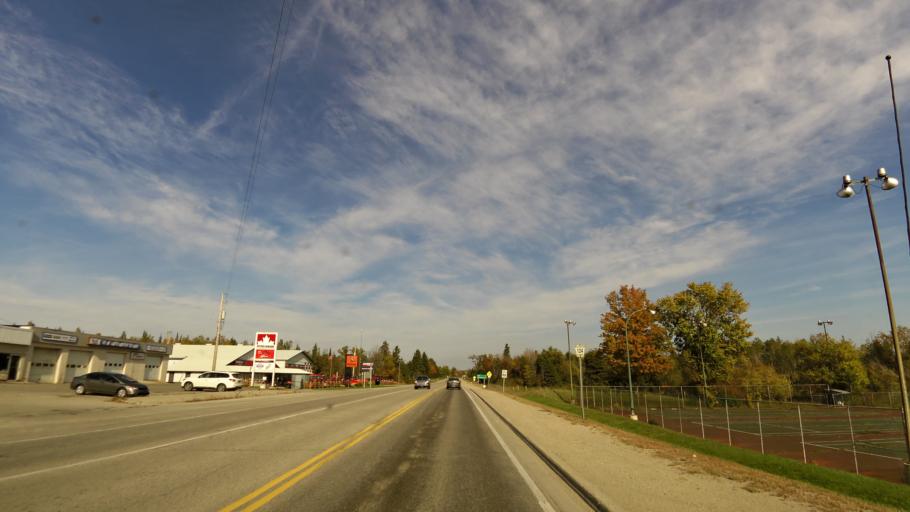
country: CA
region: Ontario
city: Orangeville
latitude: 43.7446
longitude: -80.0765
